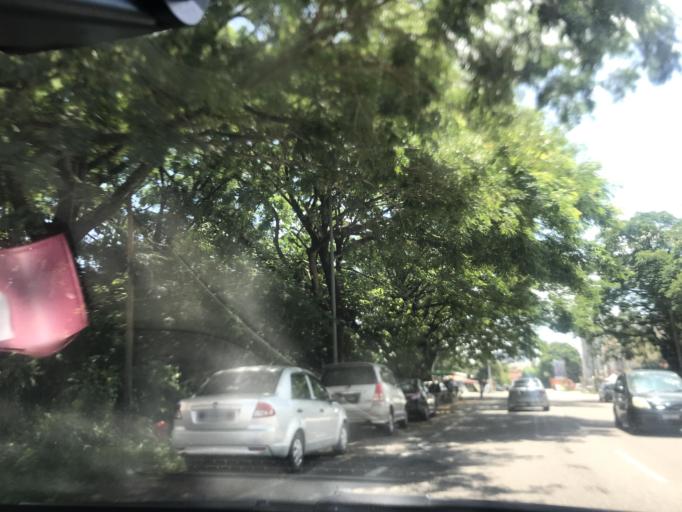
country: MY
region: Kelantan
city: Kota Bharu
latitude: 6.1306
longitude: 102.2477
